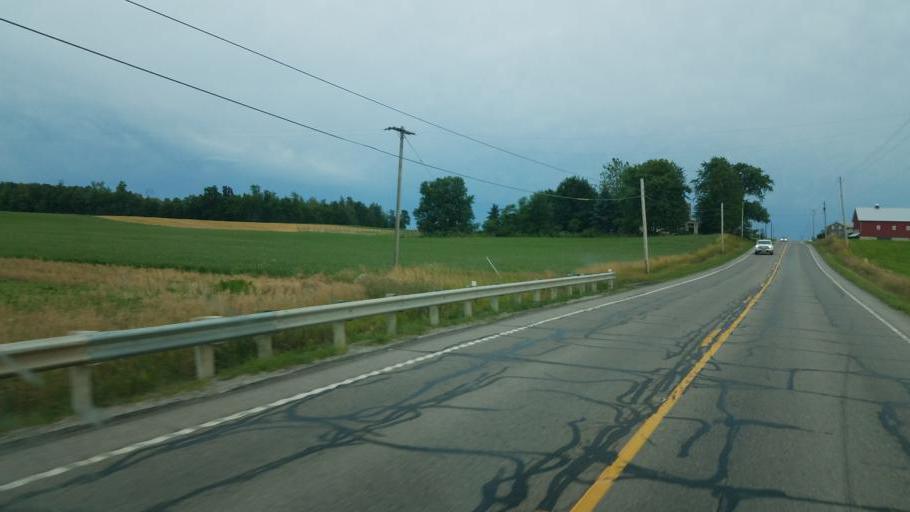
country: US
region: Ohio
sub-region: Huron County
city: Greenwich
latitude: 40.9370
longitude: -82.4952
